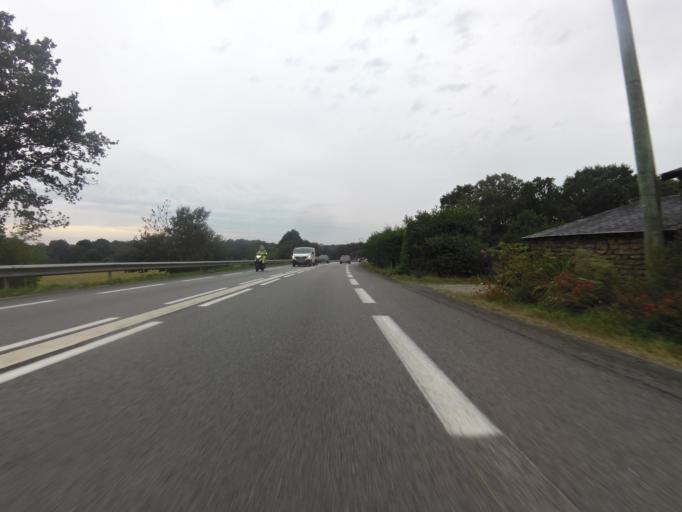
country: FR
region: Brittany
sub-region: Departement du Morbihan
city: Meucon
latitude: 47.6986
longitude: -2.7786
